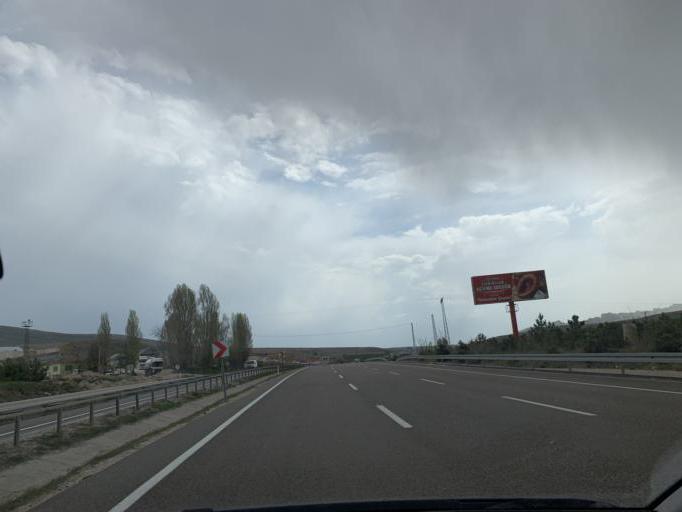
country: TR
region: Eskisehir
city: Sivrihisar
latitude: 39.4855
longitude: 31.5989
